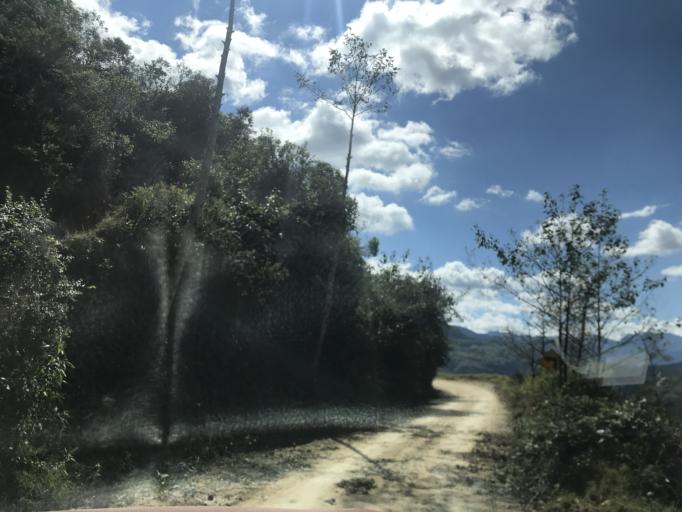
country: PE
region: Cajamarca
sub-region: Provincia de Chota
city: Querocoto
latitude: -6.3346
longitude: -79.0745
